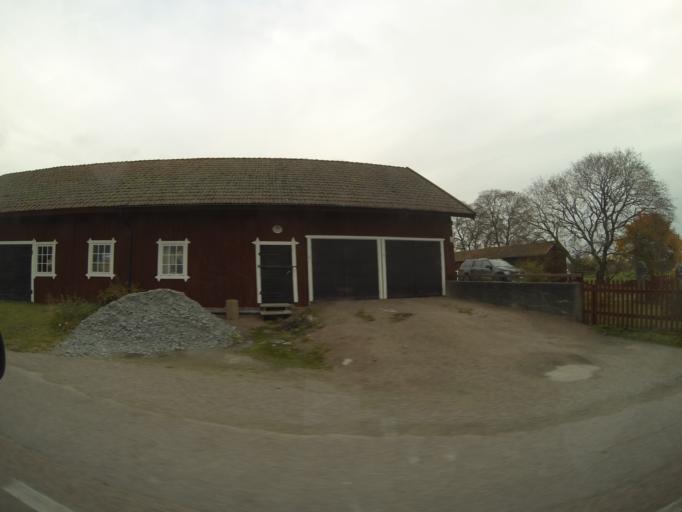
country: SE
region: Vaestmanland
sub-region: Vasteras
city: Skultuna
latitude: 59.6646
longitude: 16.4603
